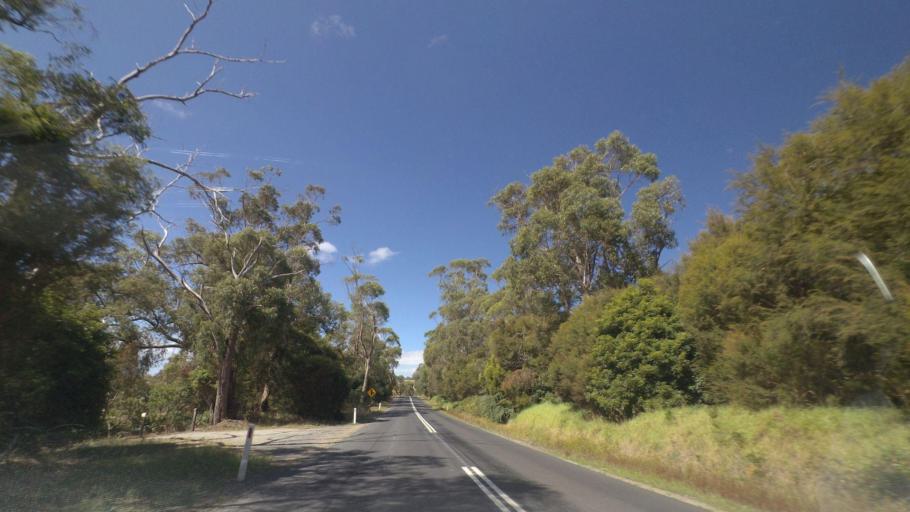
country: AU
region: Victoria
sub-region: Cardinia
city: Bunyip
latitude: -38.2461
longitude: 145.6887
